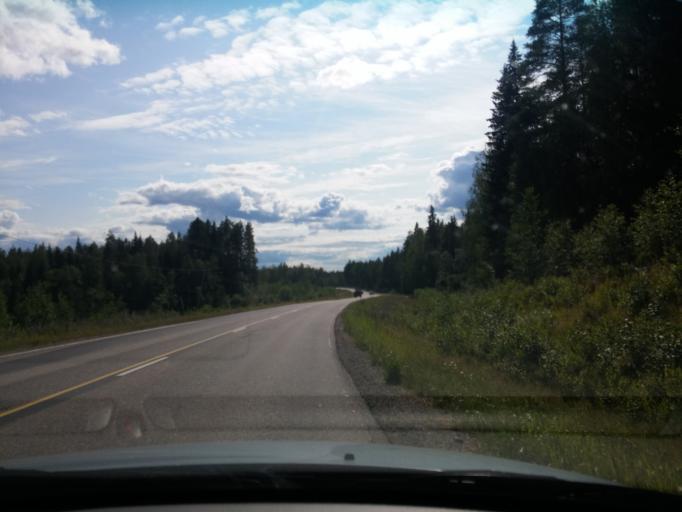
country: FI
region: Central Finland
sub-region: Keuruu
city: Keuruu
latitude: 62.2915
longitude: 24.7081
